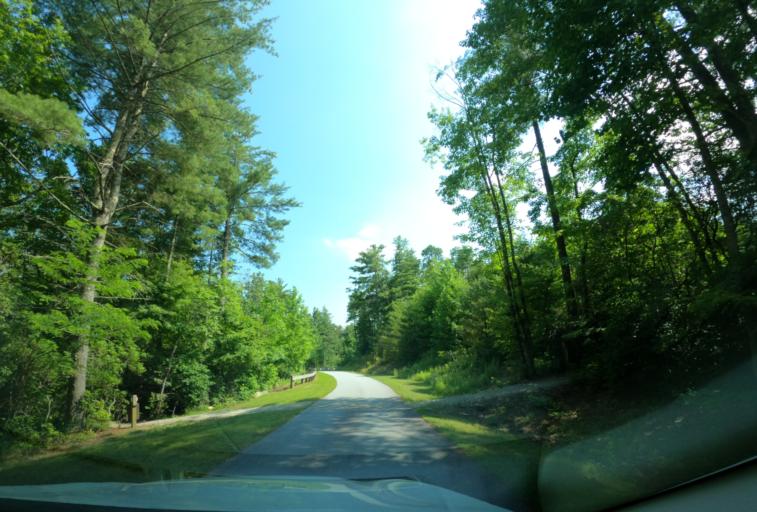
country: US
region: North Carolina
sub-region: Transylvania County
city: Brevard
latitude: 35.1015
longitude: -82.9451
